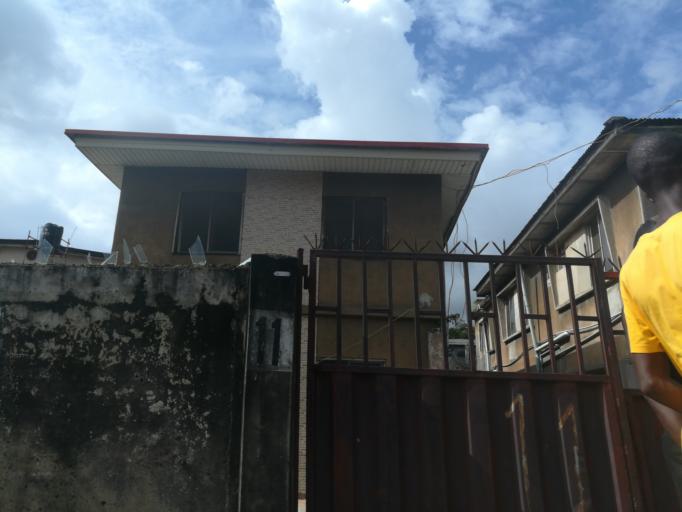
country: NG
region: Lagos
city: Somolu
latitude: 6.5493
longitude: 3.3691
